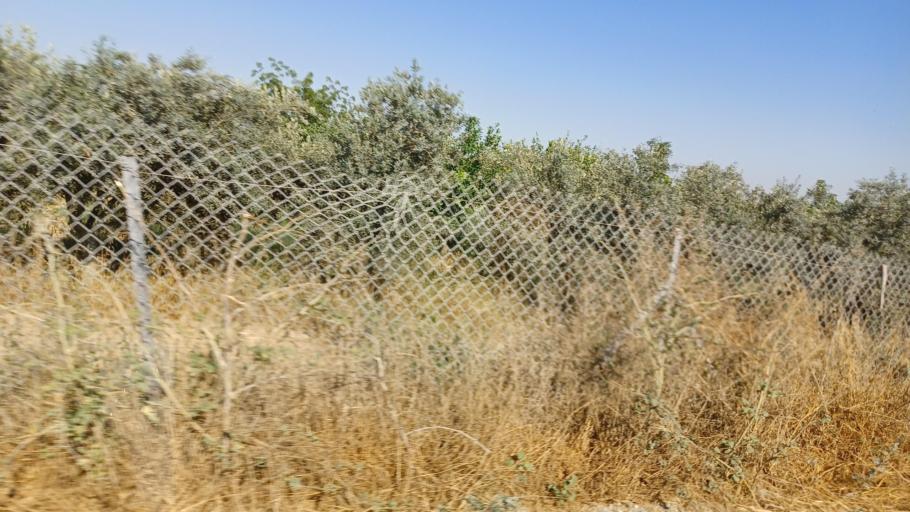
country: CY
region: Larnaka
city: Athienou
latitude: 35.0526
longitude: 33.5196
